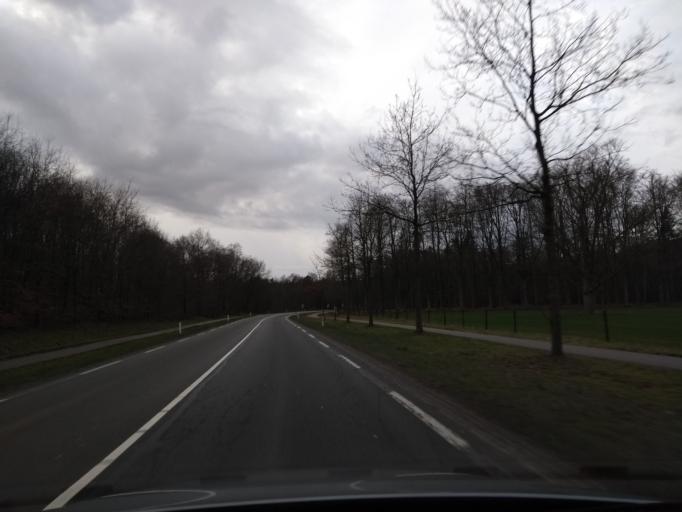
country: NL
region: Overijssel
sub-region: Gemeente Enschede
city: Enschede
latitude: 52.2781
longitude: 6.8661
